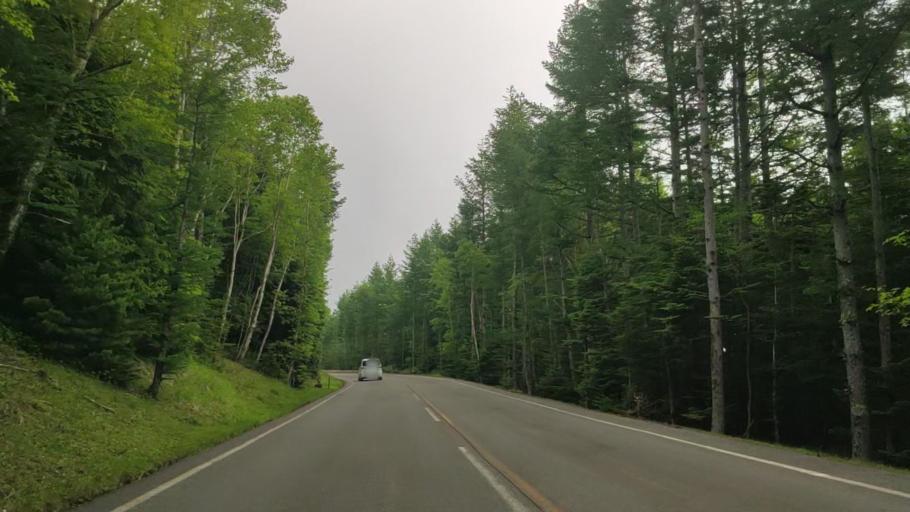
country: JP
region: Yamanashi
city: Fujikawaguchiko
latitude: 35.3793
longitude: 138.6907
